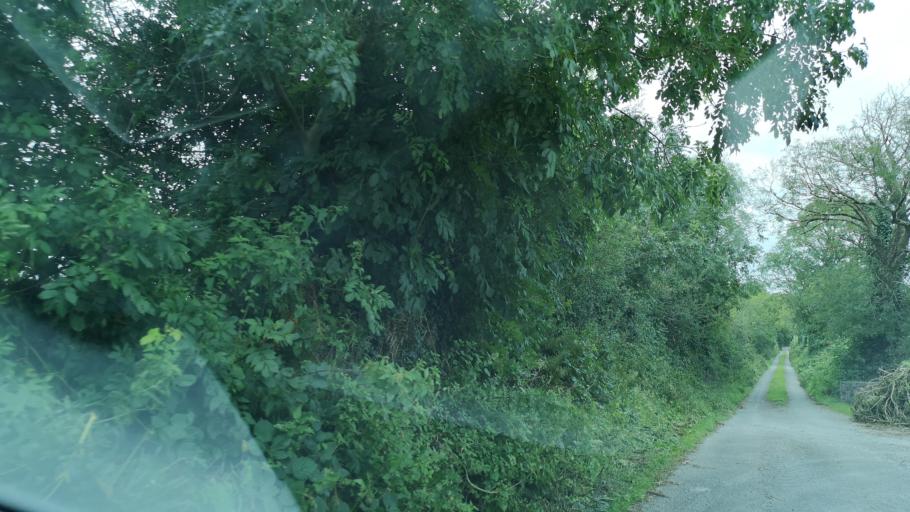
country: IE
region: Connaught
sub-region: County Galway
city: Loughrea
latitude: 53.1560
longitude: -8.4400
